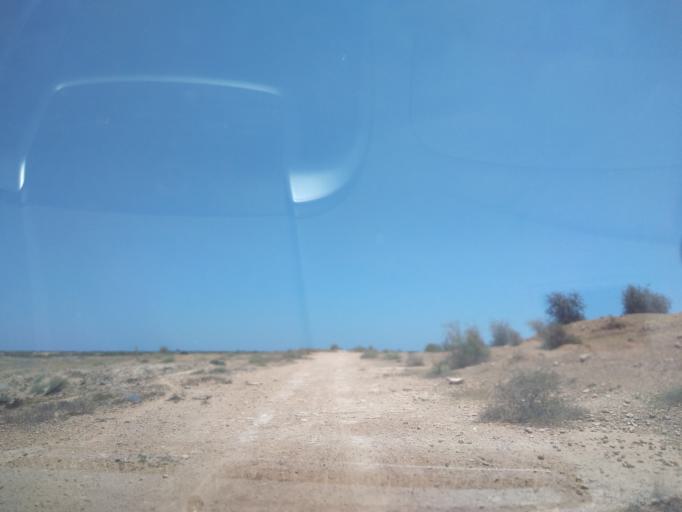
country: TN
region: Susah
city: Harqalah
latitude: 36.1707
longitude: 10.4442
